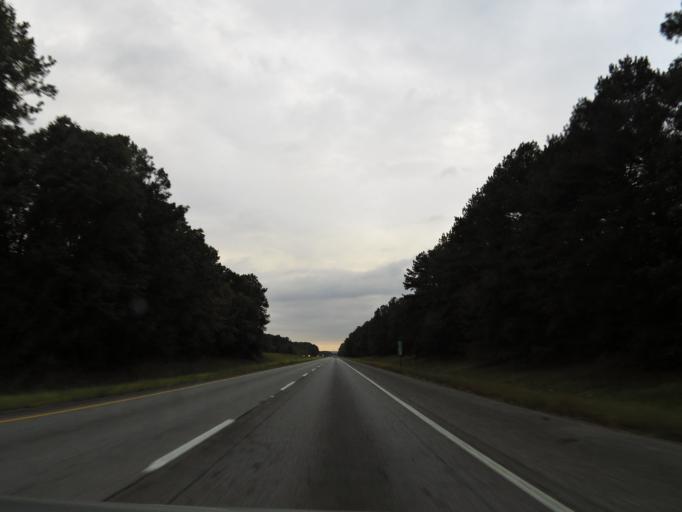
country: US
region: Alabama
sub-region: Saint Clair County
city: Ashville
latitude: 33.8335
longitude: -86.3319
